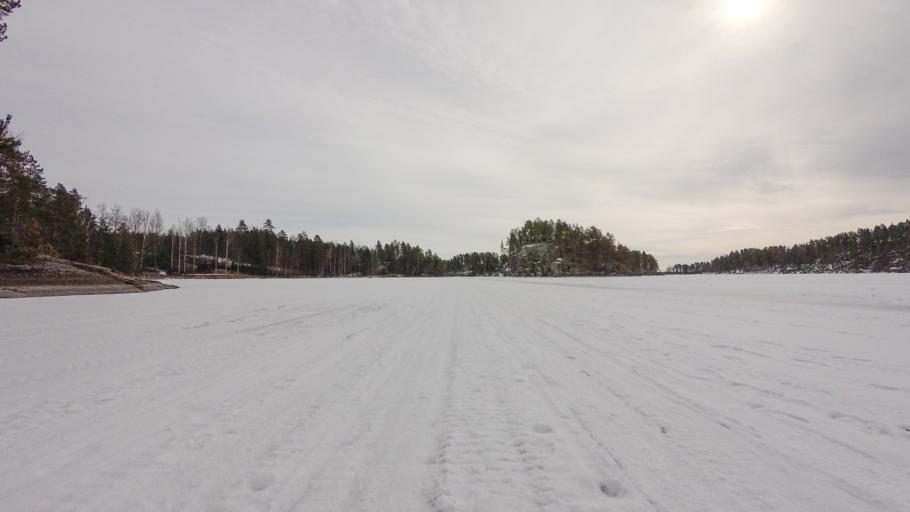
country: FI
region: Southern Savonia
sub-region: Savonlinna
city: Rantasalmi
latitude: 62.1161
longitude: 28.3190
